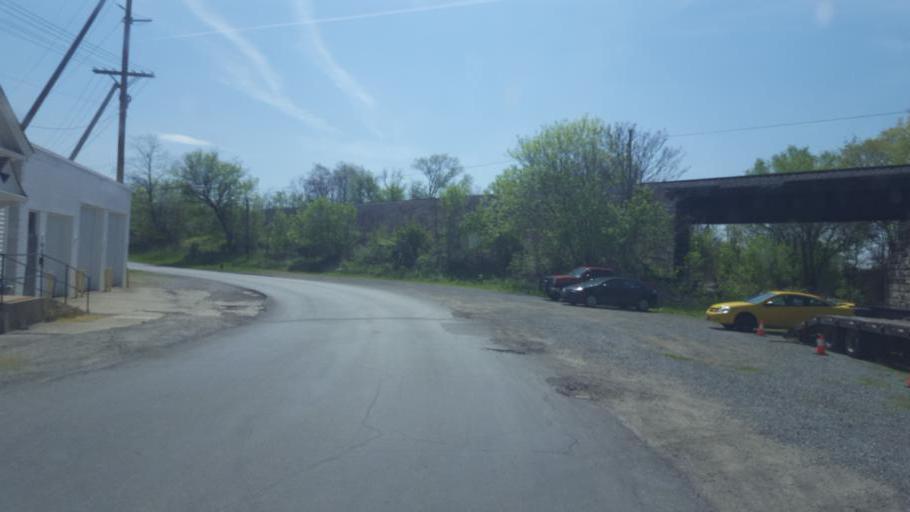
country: US
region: Ohio
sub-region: Medina County
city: Lodi
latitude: 41.0301
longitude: -82.0121
